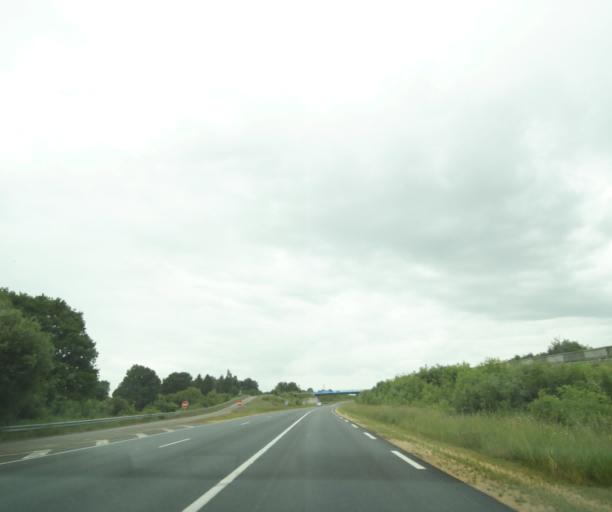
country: FR
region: Poitou-Charentes
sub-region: Departement des Deux-Sevres
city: Parthenay
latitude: 46.6508
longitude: -0.2703
